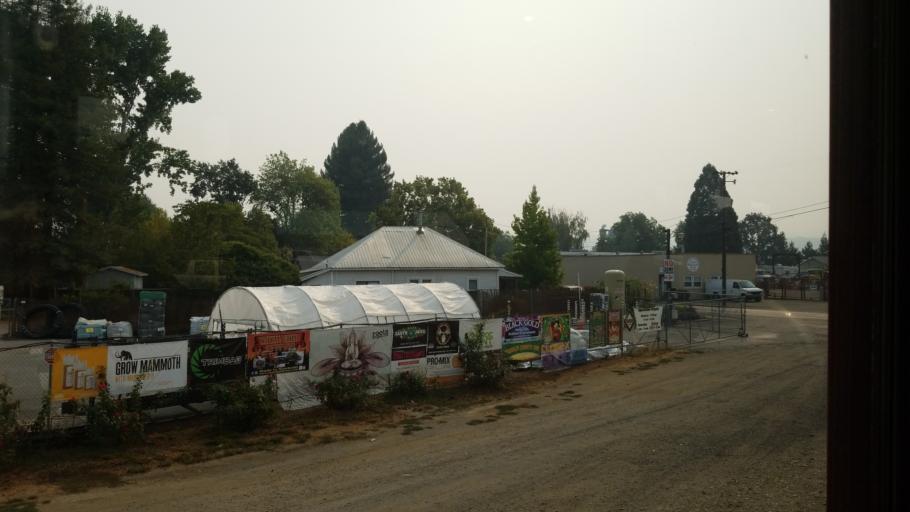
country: US
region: California
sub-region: Mendocino County
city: Willits
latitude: 39.4078
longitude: -123.3492
